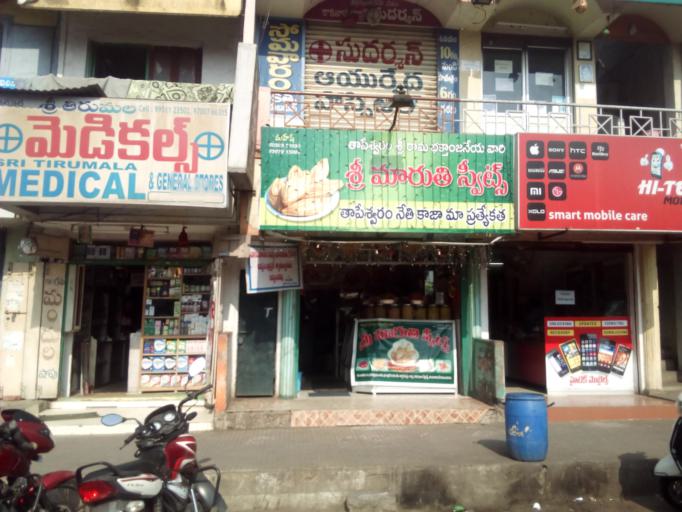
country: IN
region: Andhra Pradesh
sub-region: East Godavari
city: Rajahmundry
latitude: 16.9946
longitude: 81.7752
